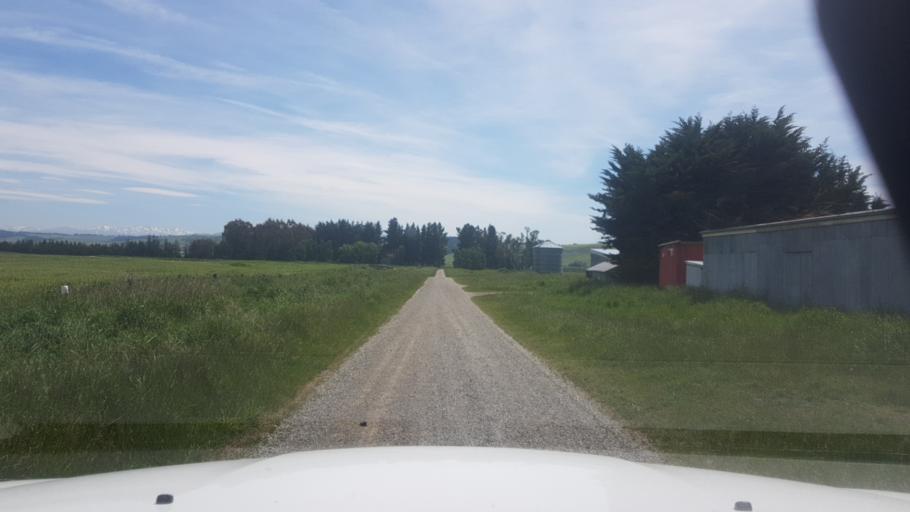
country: NZ
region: Canterbury
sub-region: Timaru District
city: Pleasant Point
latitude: -44.2245
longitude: 171.1641
